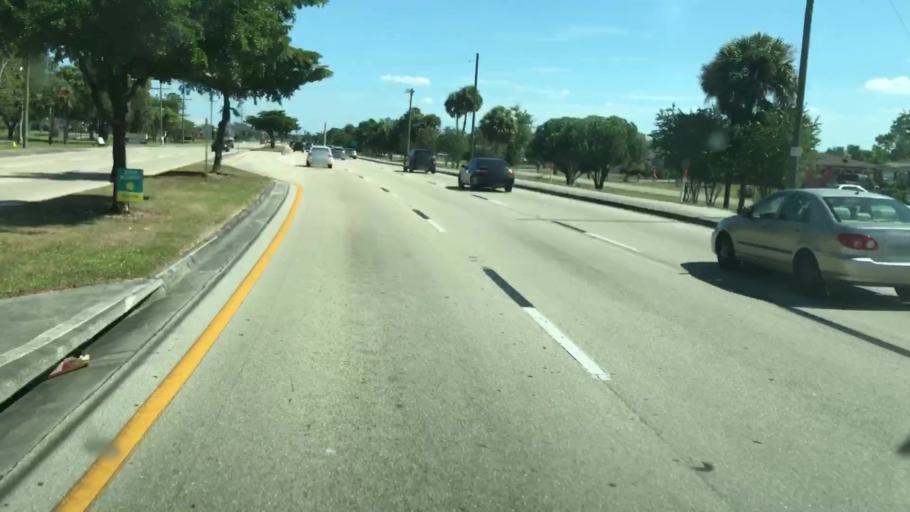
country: US
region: Florida
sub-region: Lee County
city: Lehigh Acres
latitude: 26.6141
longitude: -81.6620
